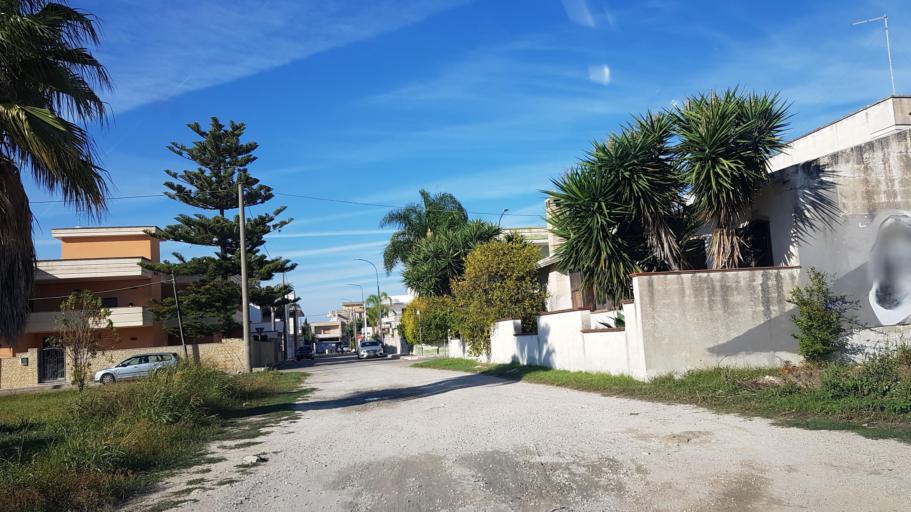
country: IT
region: Apulia
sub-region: Provincia di Lecce
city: Salice Salentino
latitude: 40.3863
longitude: 17.9565
